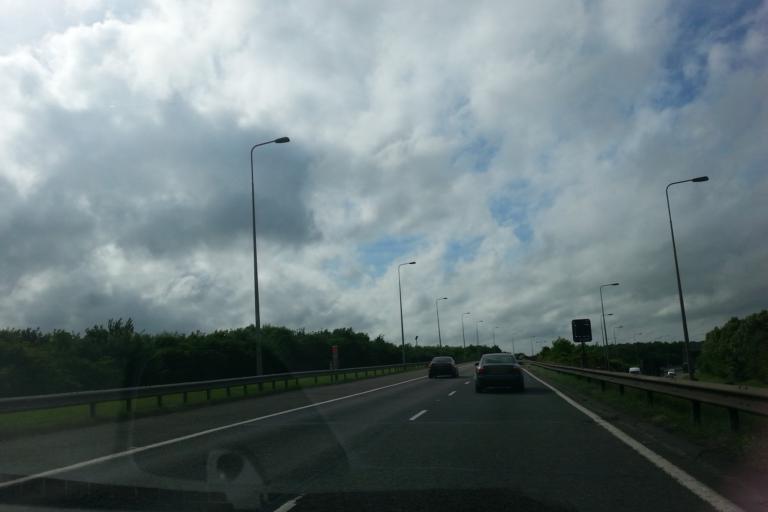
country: GB
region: England
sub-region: Cambridgeshire
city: Great Stukeley
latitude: 52.3774
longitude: -0.2529
